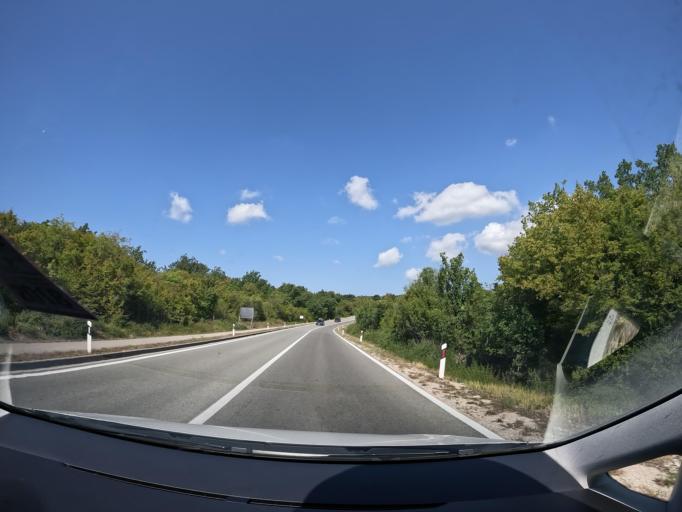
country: HR
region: Primorsko-Goranska
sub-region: Grad Krk
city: Krk
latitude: 45.0531
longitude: 14.5596
